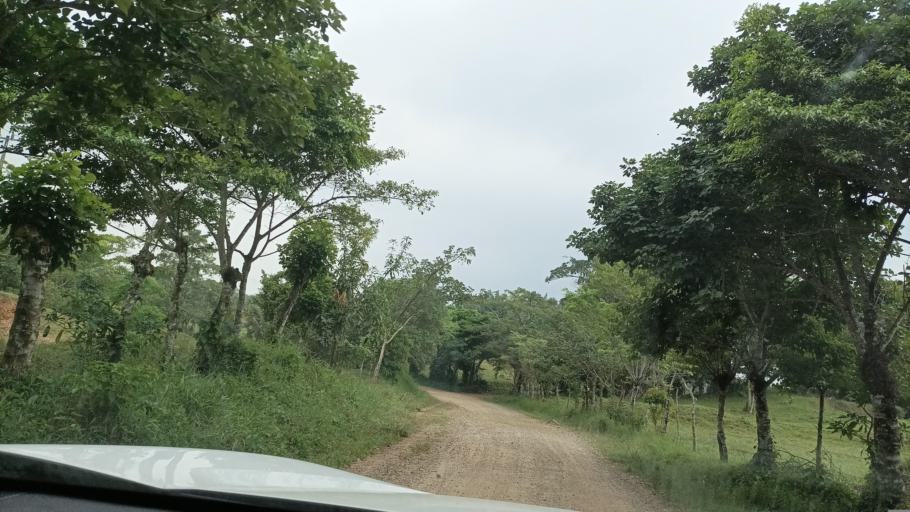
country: MX
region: Veracruz
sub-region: Uxpanapa
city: Poblado 10
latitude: 17.5480
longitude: -94.2270
